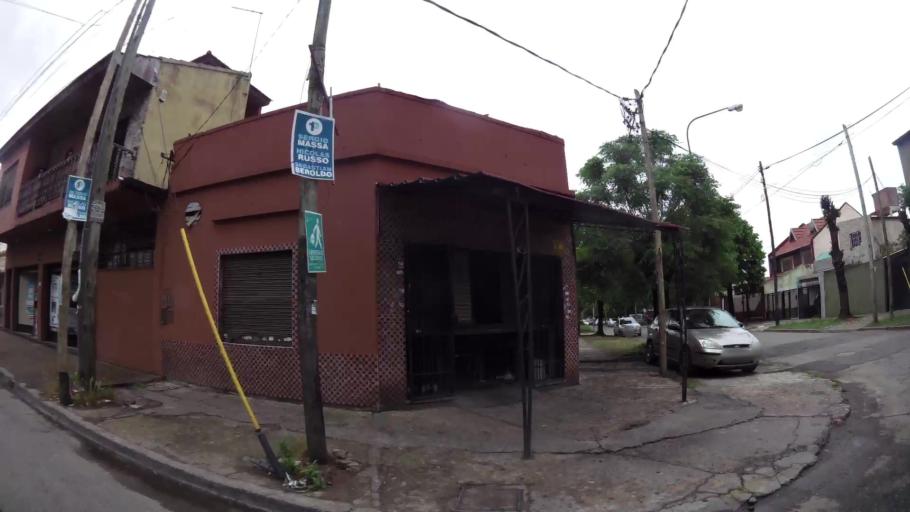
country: AR
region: Buenos Aires
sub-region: Partido de Lanus
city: Lanus
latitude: -34.7283
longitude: -58.3695
